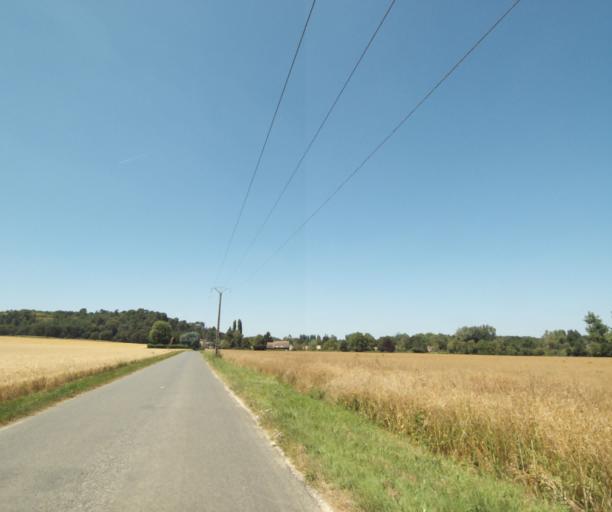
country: FR
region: Ile-de-France
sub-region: Departement de Seine-et-Marne
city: Noisy-sur-Ecole
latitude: 48.3616
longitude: 2.5120
